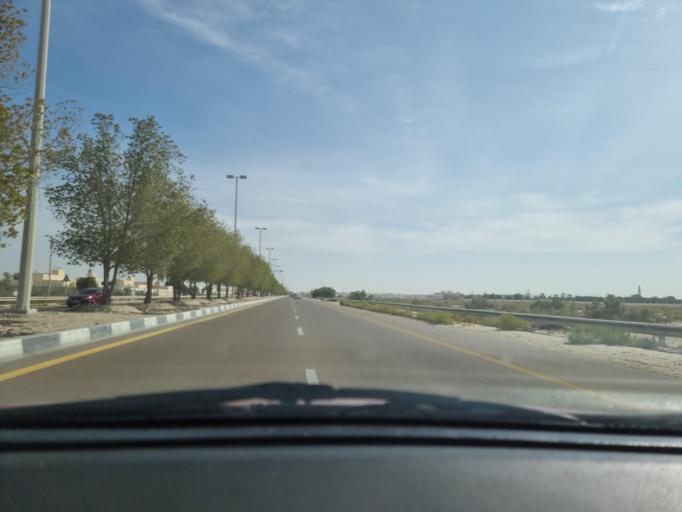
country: AE
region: Abu Dhabi
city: Abu Dhabi
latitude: 24.3837
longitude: 54.6838
